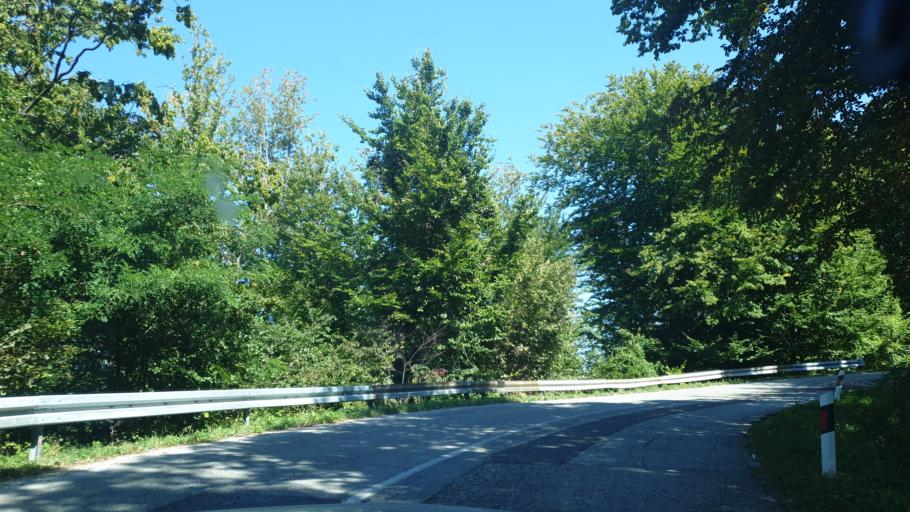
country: RS
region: Central Serbia
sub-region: Kolubarski Okrug
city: Mionica
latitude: 44.1594
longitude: 19.9877
